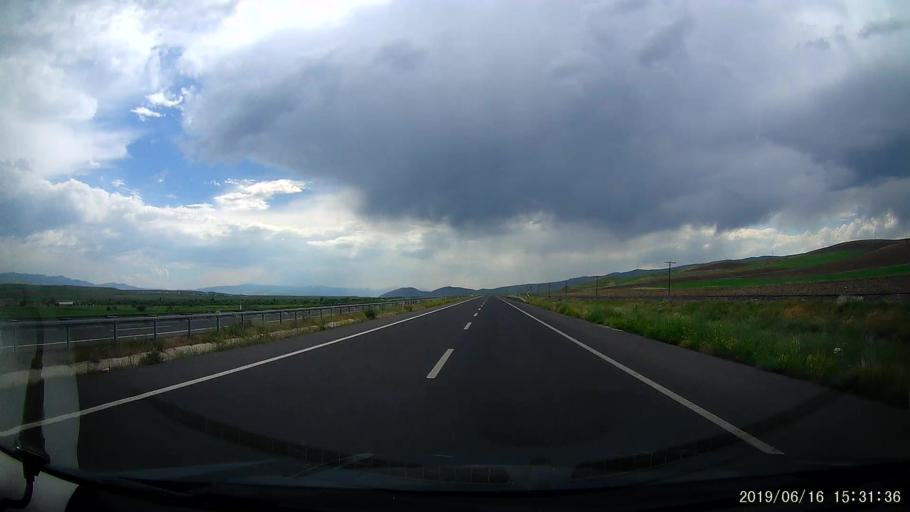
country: TR
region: Erzurum
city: Horasan
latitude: 40.0318
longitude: 42.0737
